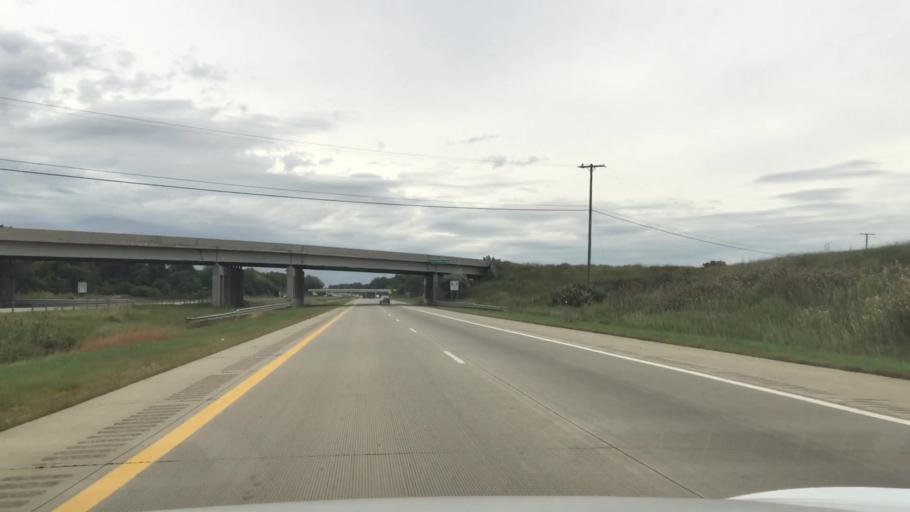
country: US
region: Michigan
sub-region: Macomb County
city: Richmond
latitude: 42.8139
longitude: -82.6272
